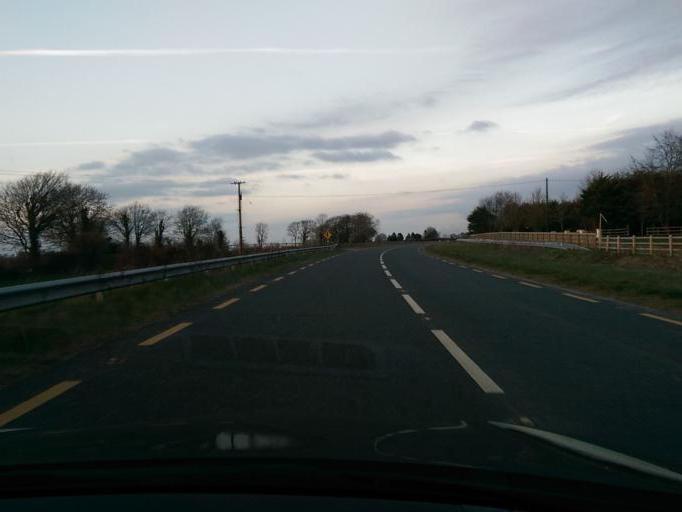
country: IE
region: Munster
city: Nenagh Bridge
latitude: 52.9543
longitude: -8.1401
